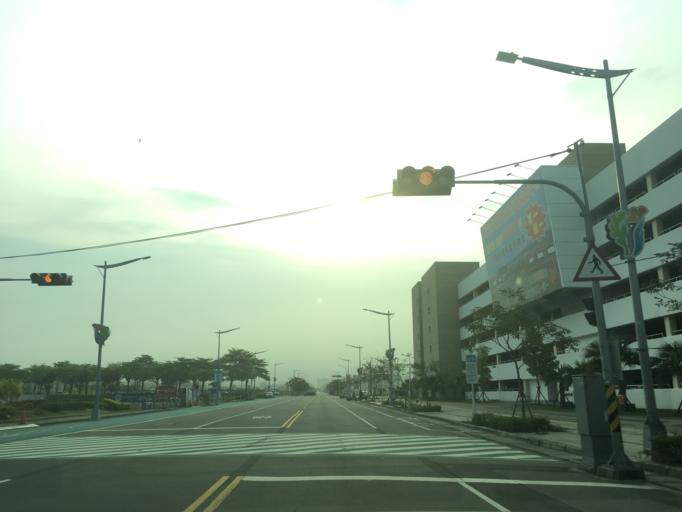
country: TW
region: Taiwan
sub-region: Taichung City
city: Taichung
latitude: 24.1978
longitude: 120.6846
